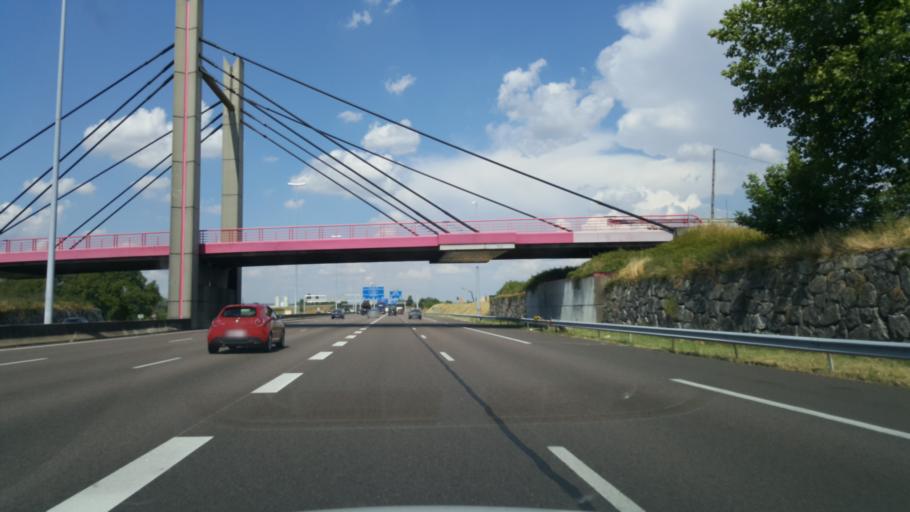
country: FR
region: Bourgogne
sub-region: Departement de la Cote-d'Or
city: Beaune
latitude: 47.0127
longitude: 4.8664
